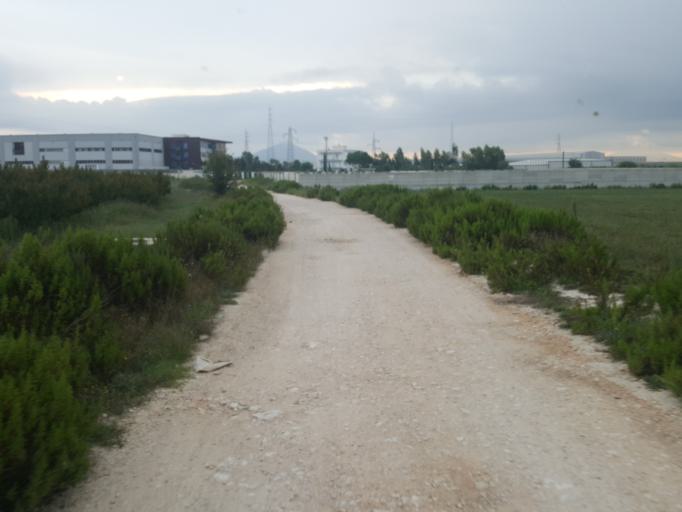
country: IT
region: Campania
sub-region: Provincia di Caserta
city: Pignataro Maggiore
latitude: 41.1729
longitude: 14.1539
